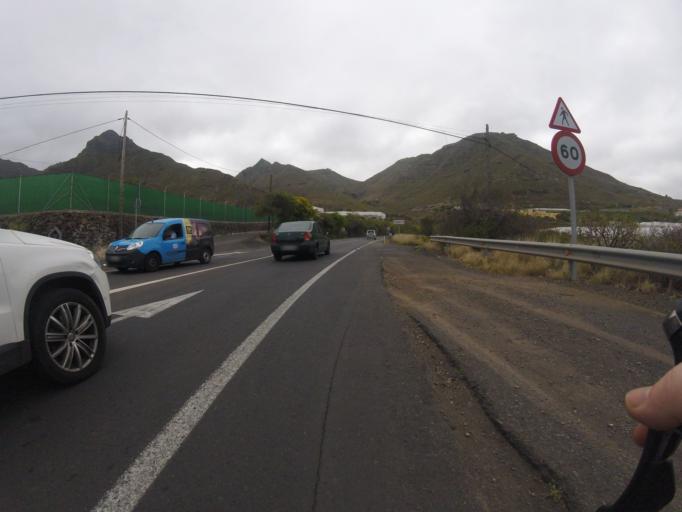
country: ES
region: Canary Islands
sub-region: Provincia de Santa Cruz de Tenerife
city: Tegueste
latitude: 28.5483
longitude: -16.3500
